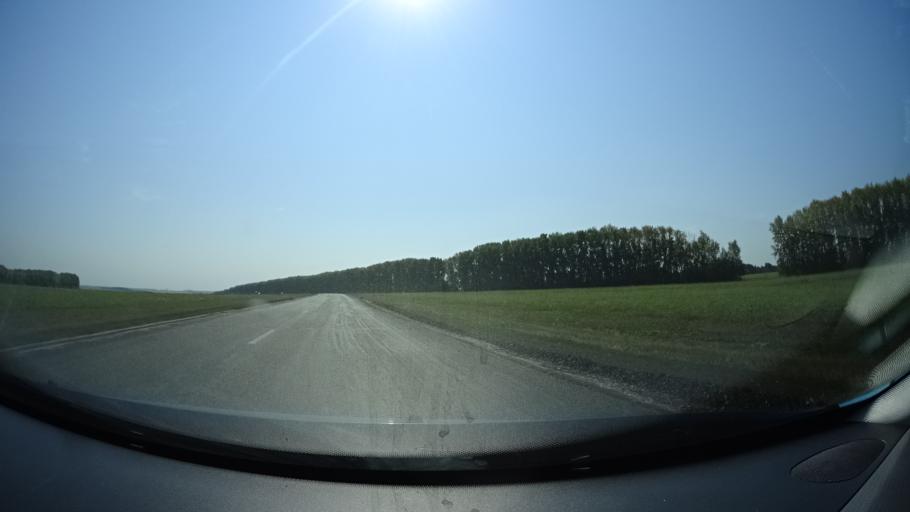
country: RU
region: Bashkortostan
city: Kabakovo
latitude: 54.4535
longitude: 55.9720
